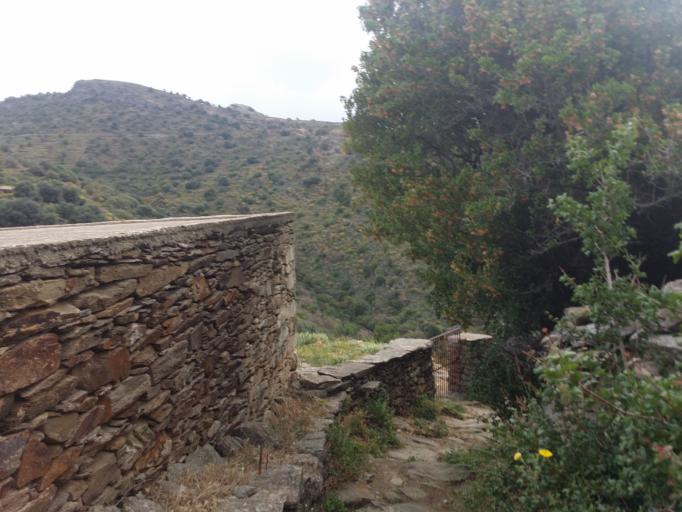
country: GR
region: South Aegean
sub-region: Nomos Kykladon
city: Kea
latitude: 37.5703
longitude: 24.3169
